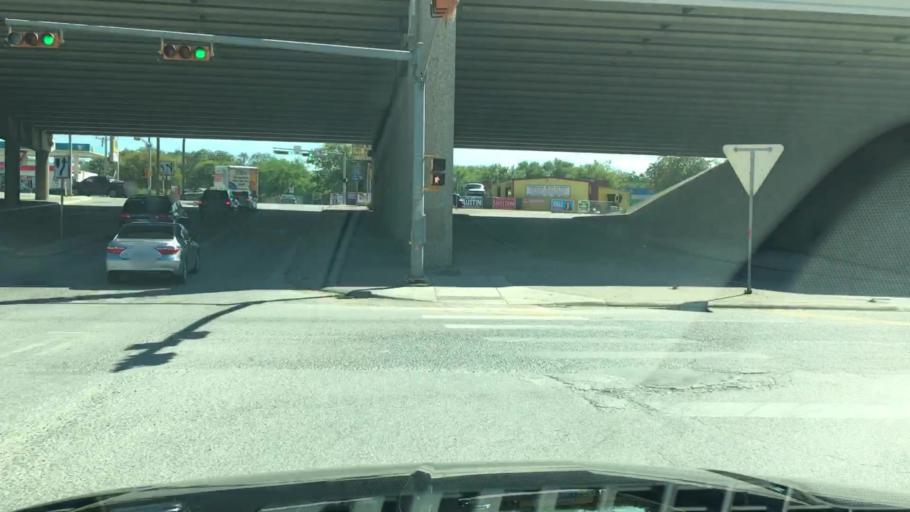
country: US
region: Texas
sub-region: Bexar County
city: Windcrest
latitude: 29.5334
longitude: -98.3899
